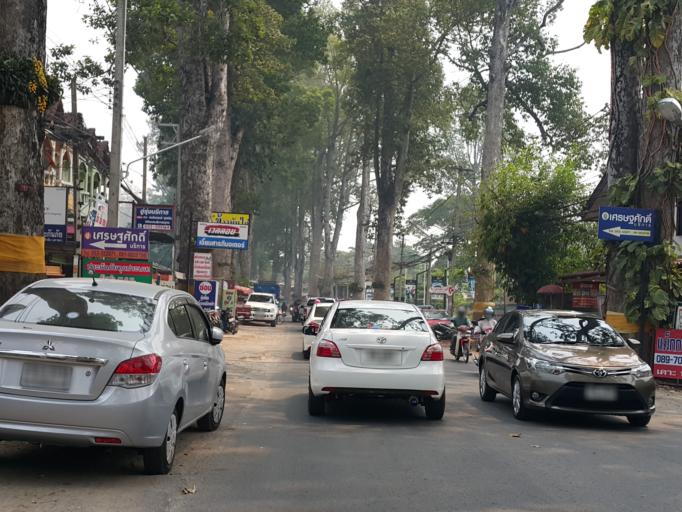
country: TH
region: Chiang Mai
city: Saraphi
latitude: 18.7380
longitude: 99.0151
